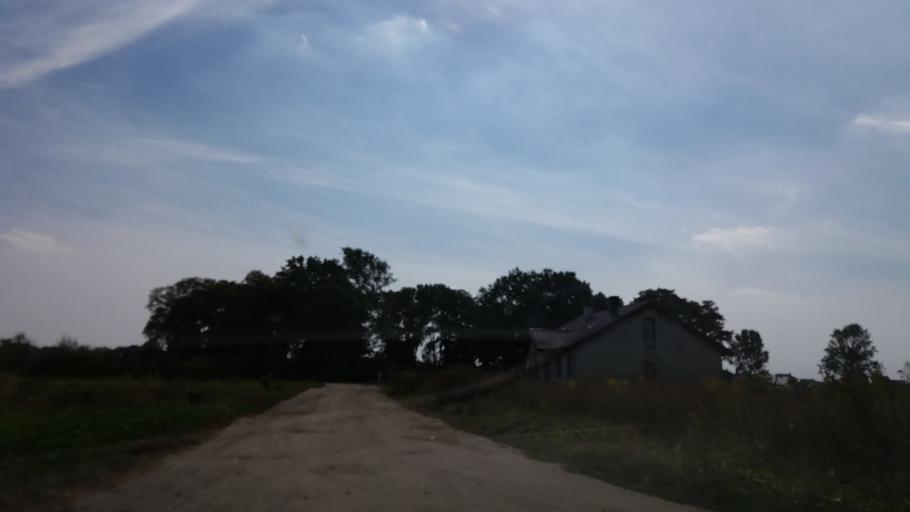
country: PL
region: West Pomeranian Voivodeship
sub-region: Powiat stargardzki
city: Stargard Szczecinski
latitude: 53.3701
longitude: 14.9684
